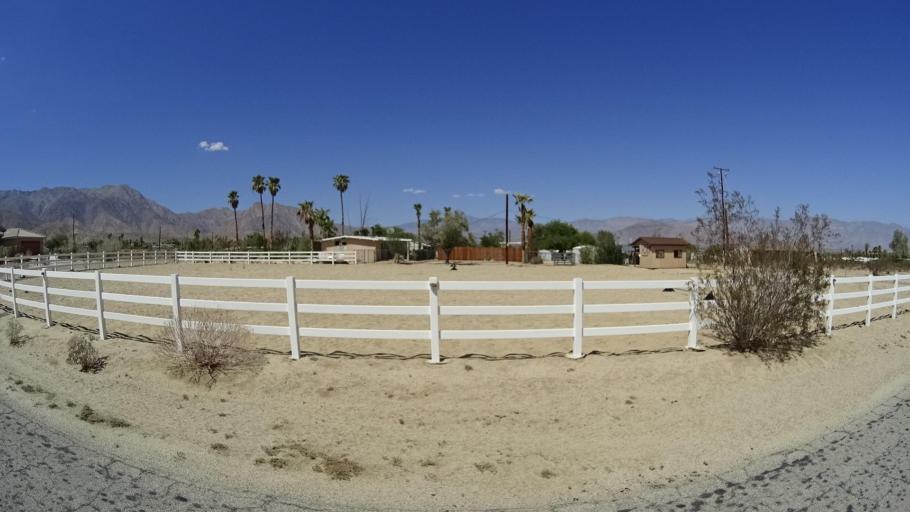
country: US
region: California
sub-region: San Diego County
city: Borrego Springs
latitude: 33.2225
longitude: -116.3705
